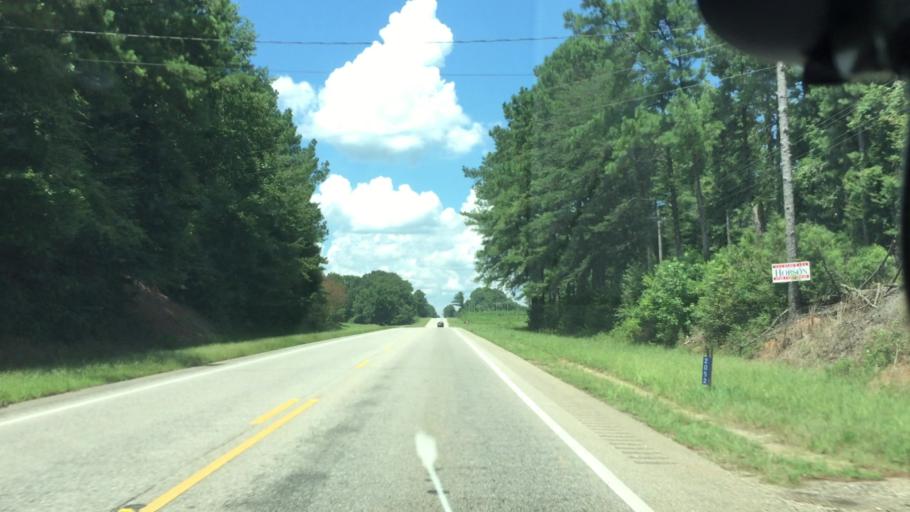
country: US
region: Alabama
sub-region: Pike County
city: Brundidge
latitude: 31.6484
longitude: -85.9492
